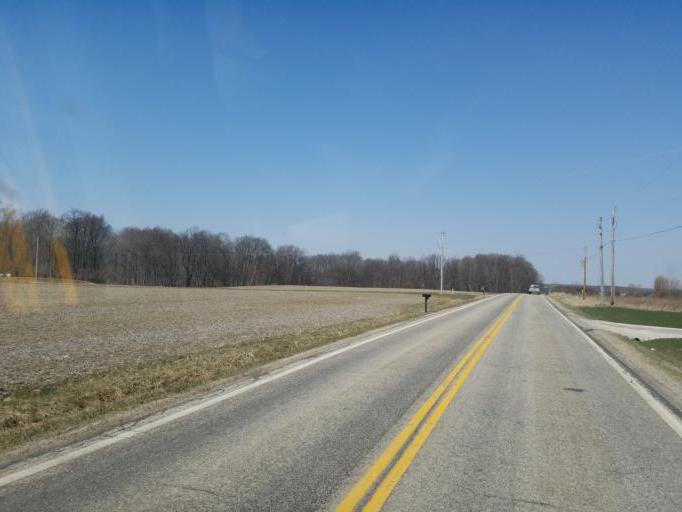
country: US
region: Ohio
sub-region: Ashland County
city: Loudonville
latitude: 40.7495
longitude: -82.2138
